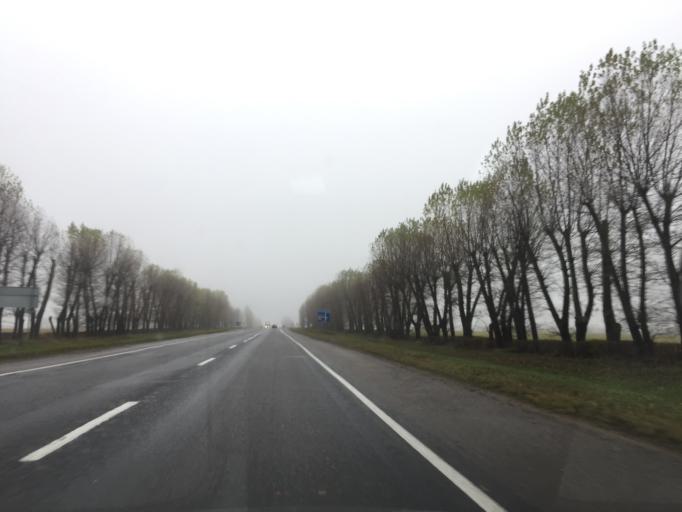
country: BY
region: Mogilev
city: Shklow
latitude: 54.1844
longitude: 30.4543
